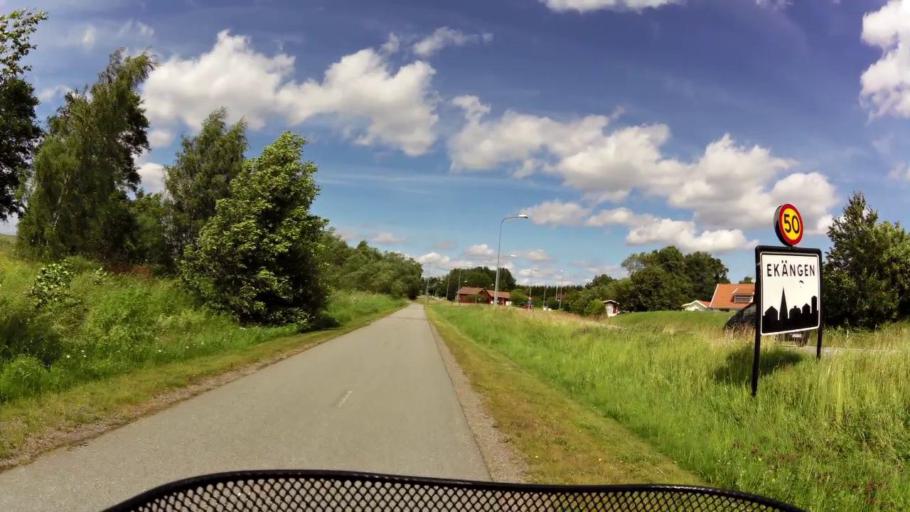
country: SE
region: OEstergoetland
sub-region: Linkopings Kommun
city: Ekangen
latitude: 58.4590
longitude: 15.6401
